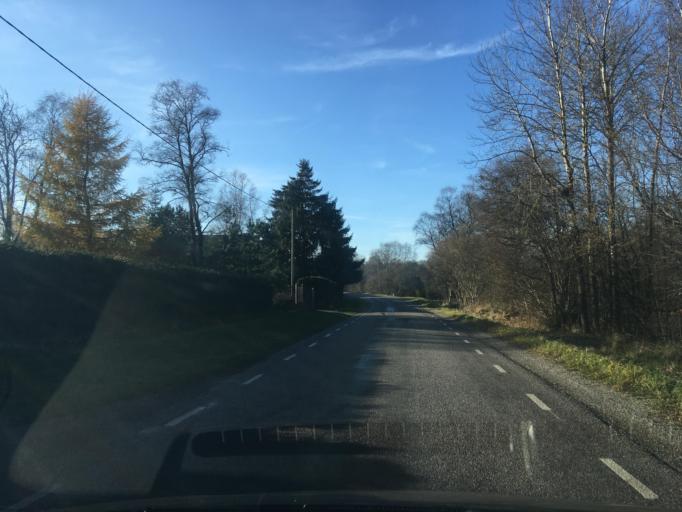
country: EE
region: Harju
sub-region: Maardu linn
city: Maardu
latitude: 59.4867
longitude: 25.0668
